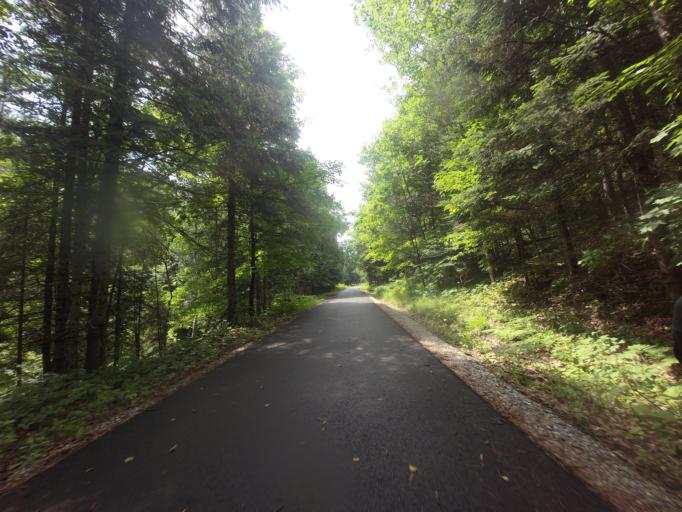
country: CA
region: Quebec
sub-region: Outaouais
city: Maniwaki
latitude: 46.1296
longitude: -76.0327
